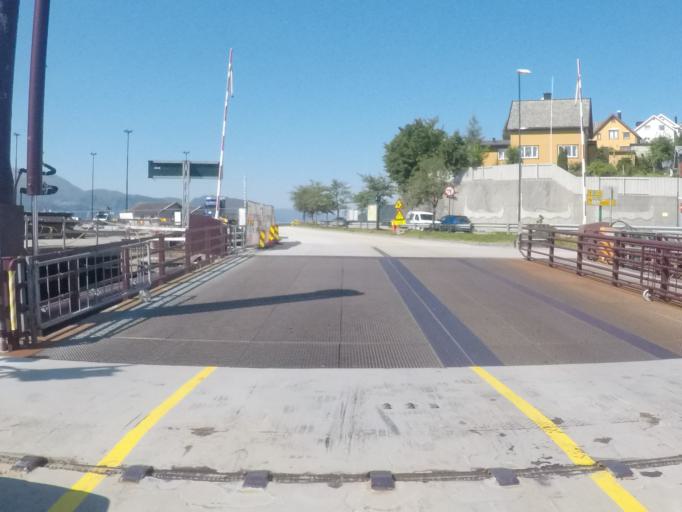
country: NO
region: More og Romsdal
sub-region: Volda
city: Volda
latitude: 62.1447
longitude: 6.0638
